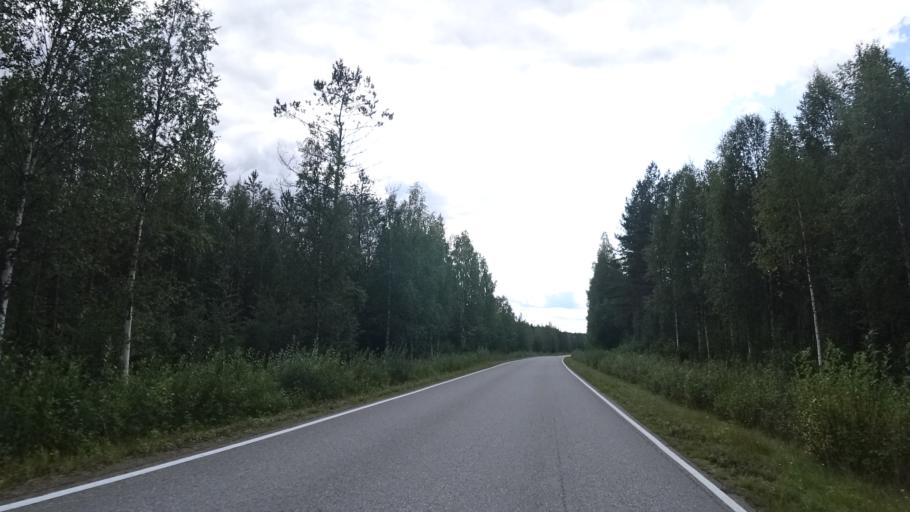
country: FI
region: North Karelia
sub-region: Joensuu
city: Ilomantsi
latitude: 62.4250
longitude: 31.0379
